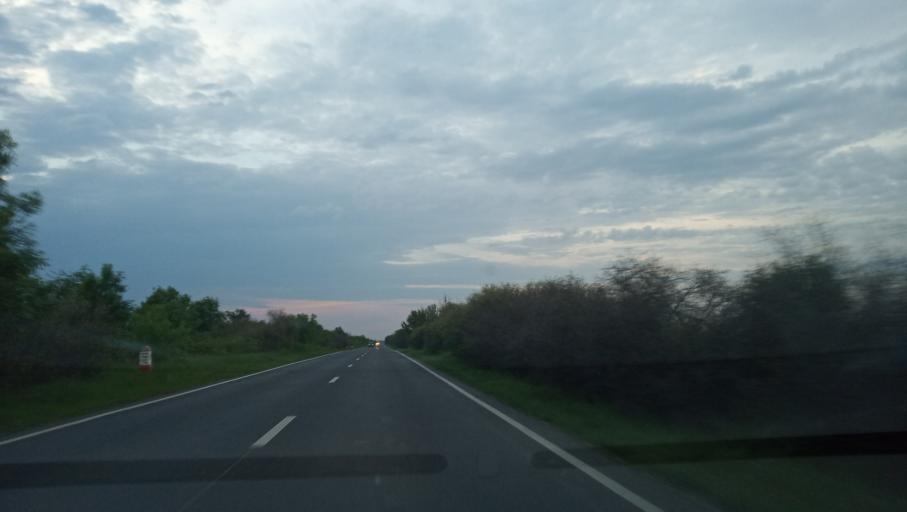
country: RO
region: Timis
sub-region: Comuna Jebel
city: Jebel
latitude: 45.5334
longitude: 21.2289
